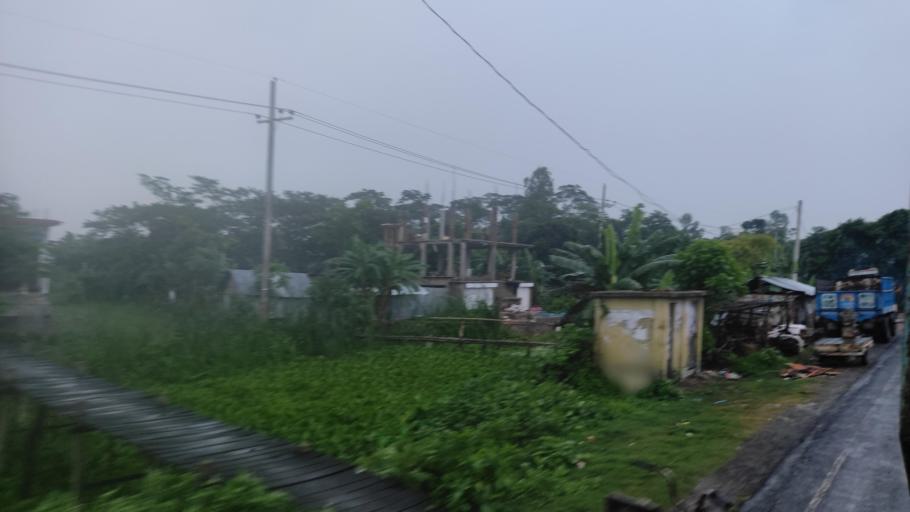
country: BD
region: Barisal
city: Bhandaria
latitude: 22.2945
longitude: 90.3251
